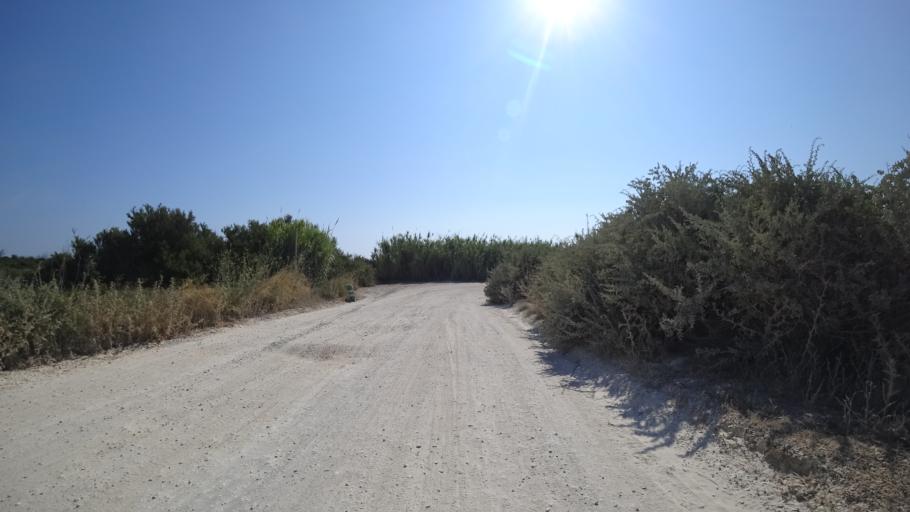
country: FR
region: Languedoc-Roussillon
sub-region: Departement des Pyrenees-Orientales
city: Le Barcares
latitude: 42.7570
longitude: 3.0277
